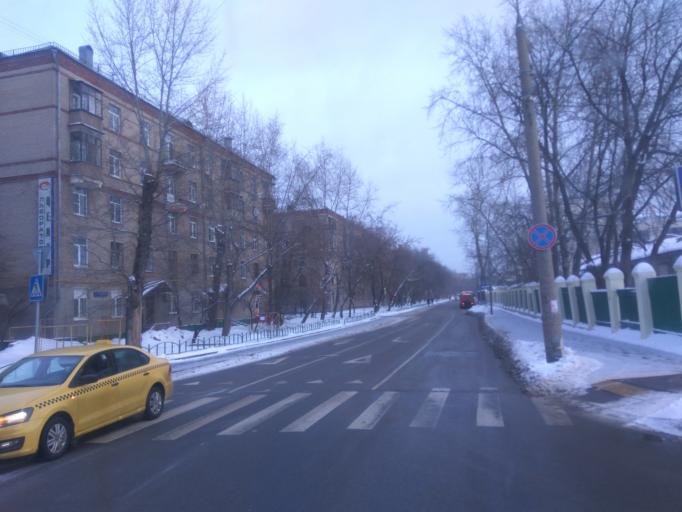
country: RU
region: Moscow
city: Mar'ina Roshcha
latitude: 55.8041
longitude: 37.5739
